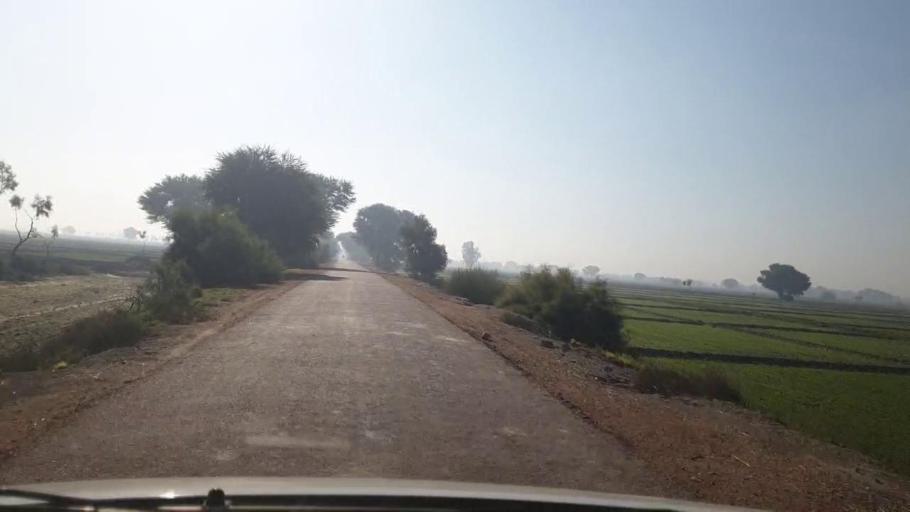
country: PK
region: Sindh
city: Dadu
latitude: 26.6657
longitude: 67.8171
